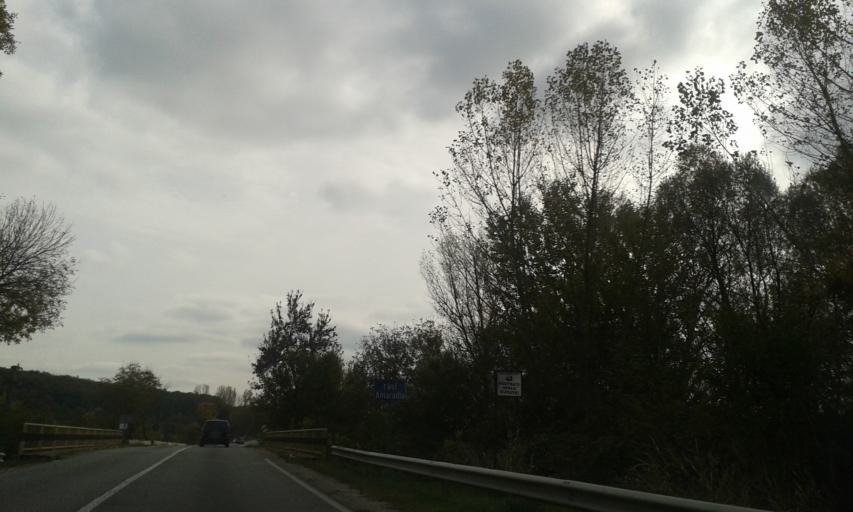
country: RO
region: Gorj
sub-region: Comuna Balanesti
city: Balanesti
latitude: 45.0377
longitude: 23.3707
